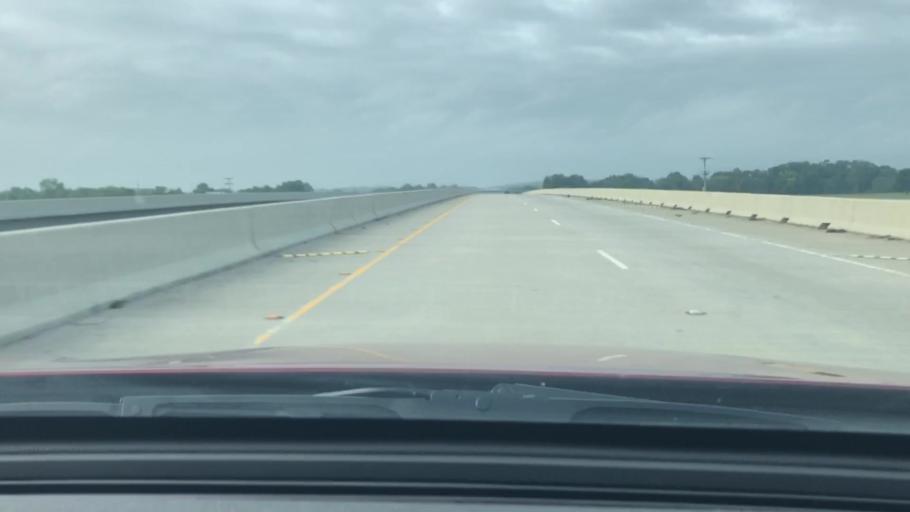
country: US
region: Louisiana
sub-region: Caddo Parish
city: Vivian
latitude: 32.8526
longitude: -93.8642
